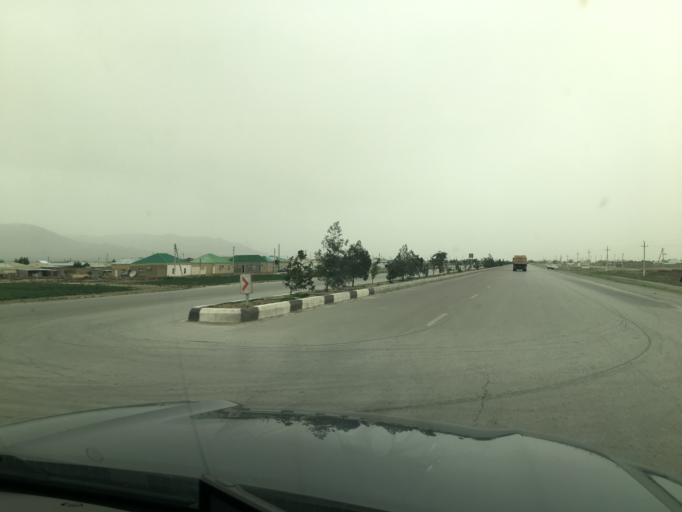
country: TM
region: Ahal
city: Baharly
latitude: 38.3935
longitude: 57.4821
